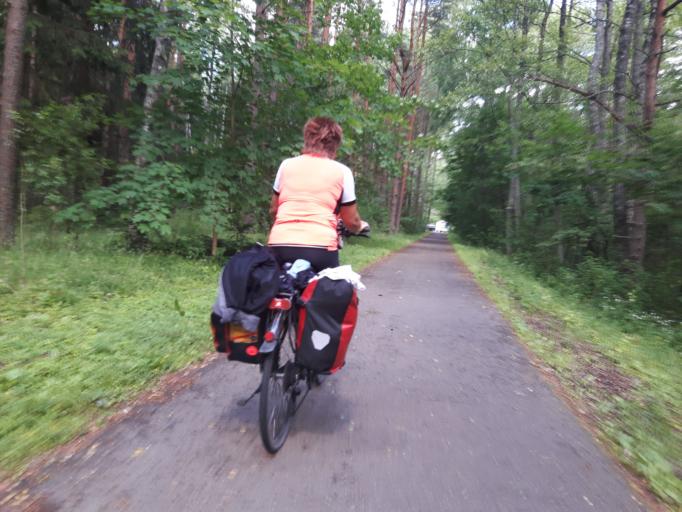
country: LT
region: Klaipedos apskritis
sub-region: Klaipeda
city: Klaipeda
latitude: 55.7938
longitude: 21.0747
